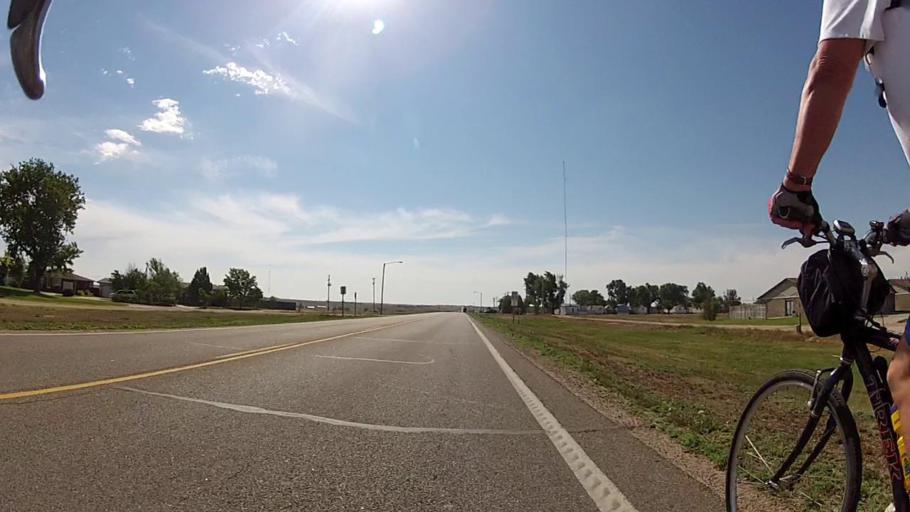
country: US
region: Kansas
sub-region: Grant County
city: Ulysses
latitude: 37.5740
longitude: -101.3415
